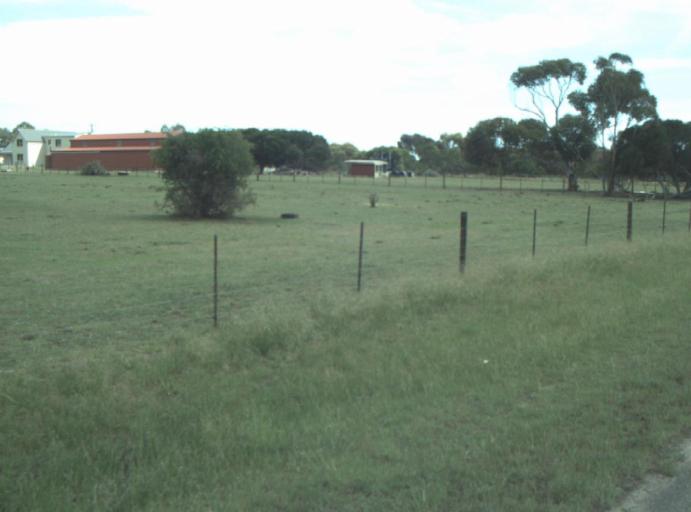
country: AU
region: Victoria
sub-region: Greater Geelong
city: Lara
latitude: -38.0429
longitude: 144.4299
